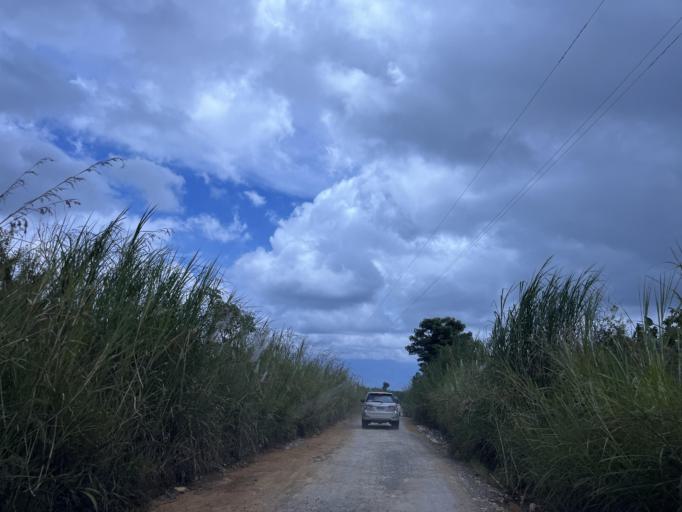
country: PH
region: Northern Mindanao
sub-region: Province of Bukidnon
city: Sumilao
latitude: 8.2183
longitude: 124.9580
